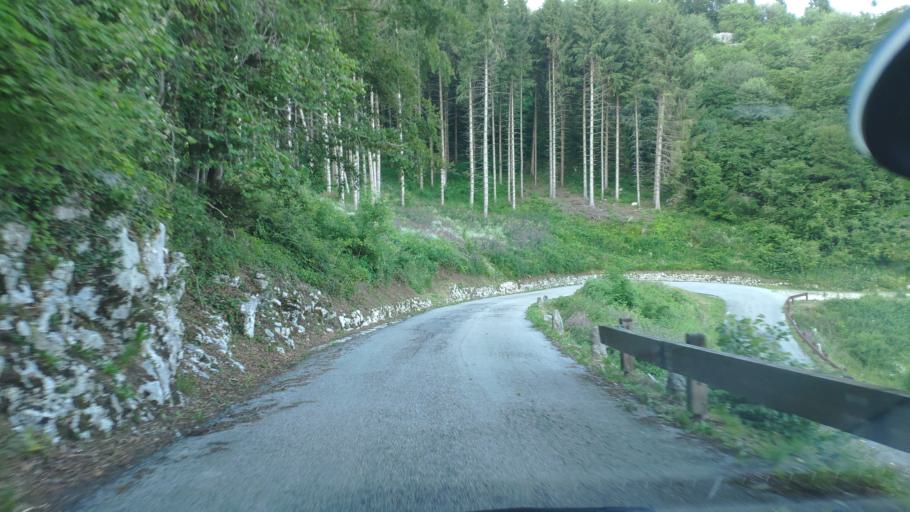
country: IT
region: Veneto
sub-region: Provincia di Vicenza
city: Calvene
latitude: 45.7903
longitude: 11.5193
